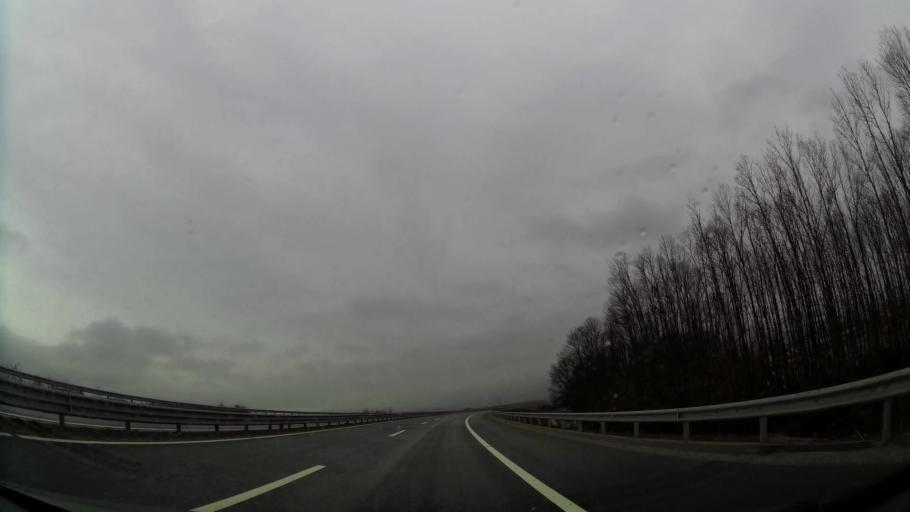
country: XK
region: Ferizaj
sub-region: Komuna e Ferizajt
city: Ferizaj
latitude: 42.3054
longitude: 21.2084
